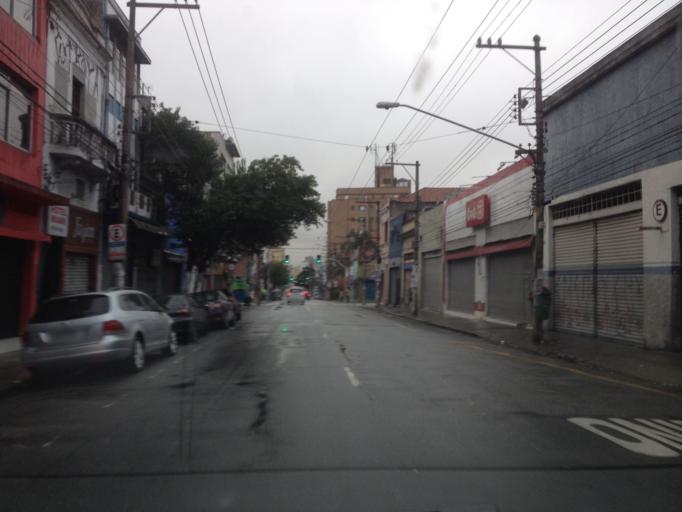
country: BR
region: Sao Paulo
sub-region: Sao Paulo
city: Sao Paulo
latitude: -23.5350
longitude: -46.6299
